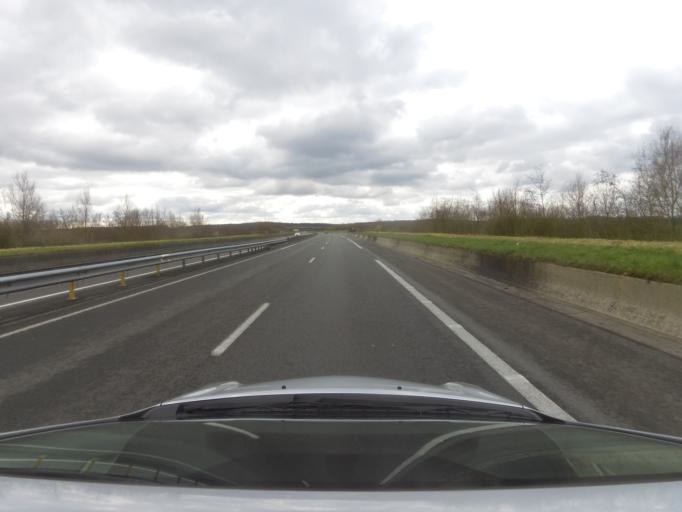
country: FR
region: Nord-Pas-de-Calais
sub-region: Departement du Pas-de-Calais
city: Saint-Josse
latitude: 50.4972
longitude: 1.6800
